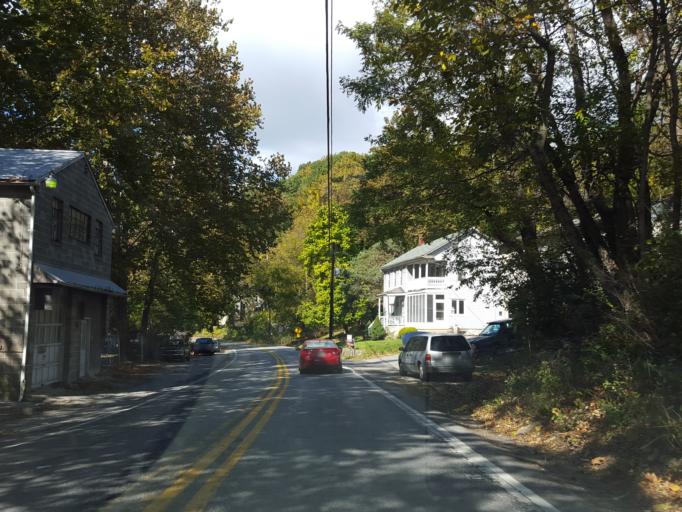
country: US
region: Pennsylvania
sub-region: York County
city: Valley View
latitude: 39.9460
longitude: -76.6733
